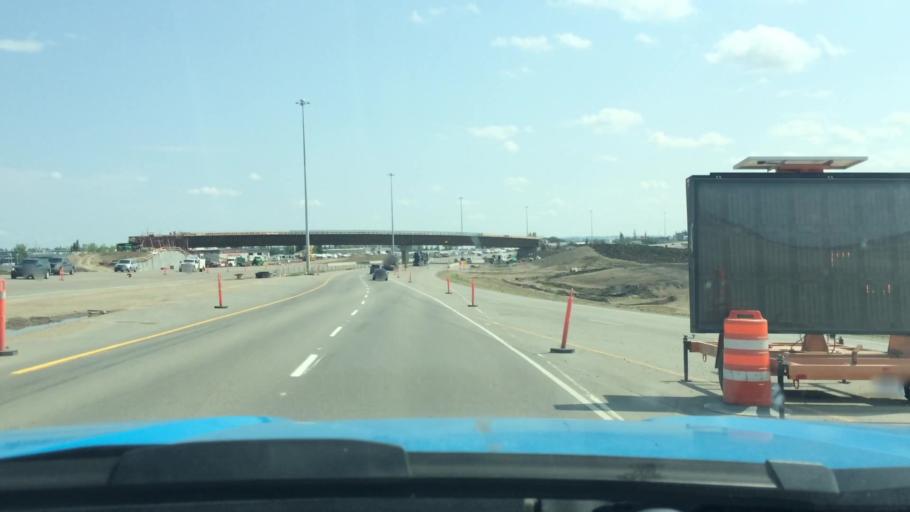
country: CA
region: Alberta
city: Red Deer
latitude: 52.2297
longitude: -113.8187
